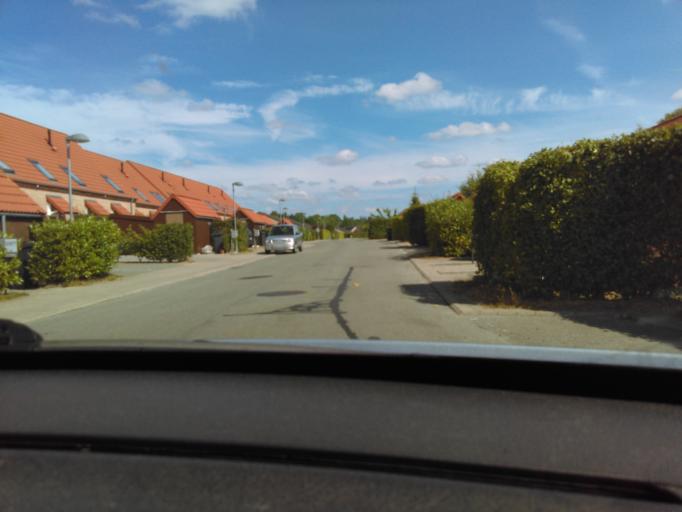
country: DK
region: Capital Region
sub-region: Fureso Kommune
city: Farum
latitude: 55.8224
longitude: 12.3529
